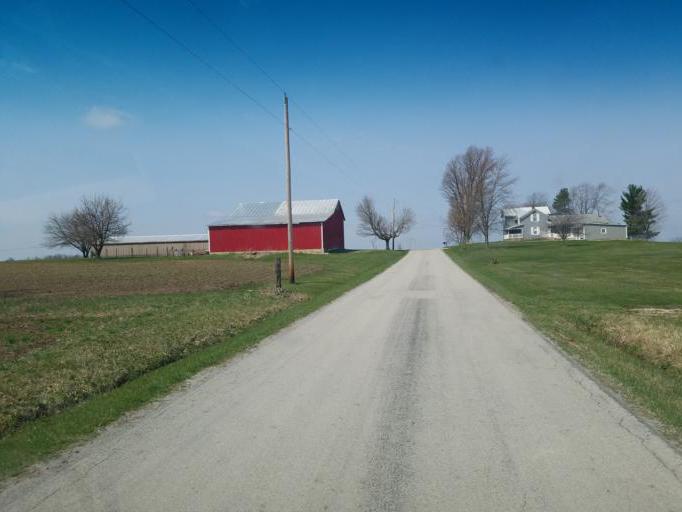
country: US
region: Ohio
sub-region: Wyandot County
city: Upper Sandusky
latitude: 40.9064
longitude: -83.1423
